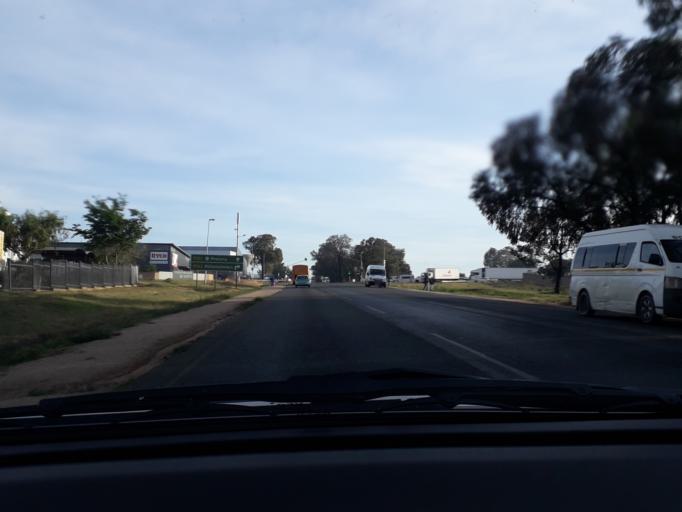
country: ZA
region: Gauteng
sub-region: City of Johannesburg Metropolitan Municipality
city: Midrand
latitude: -25.9447
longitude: 28.1435
